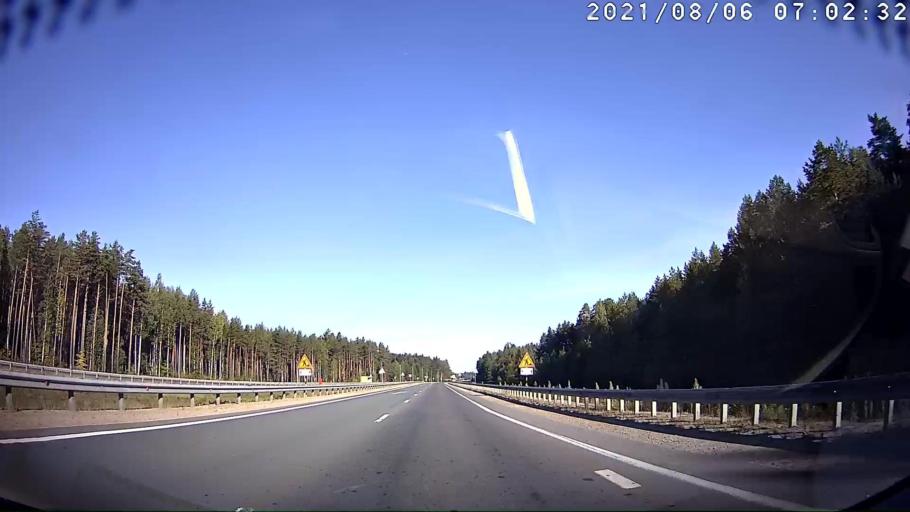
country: RU
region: Mariy-El
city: Yoshkar-Ola
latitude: 56.5350
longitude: 47.9946
